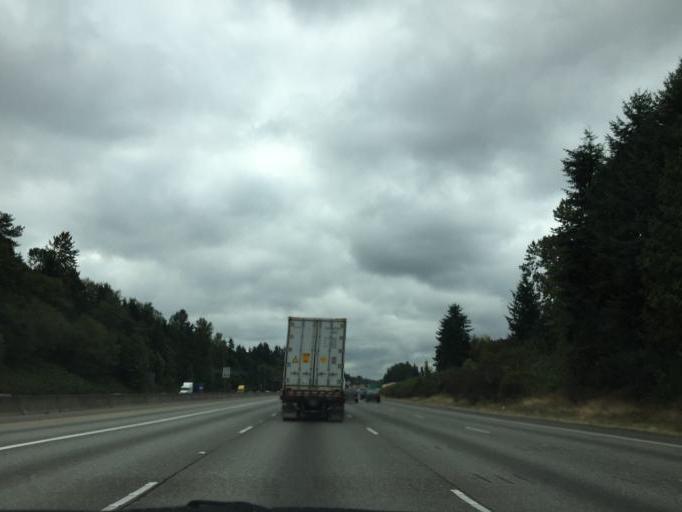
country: US
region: Washington
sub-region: King County
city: Des Moines
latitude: 47.3840
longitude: -122.2905
